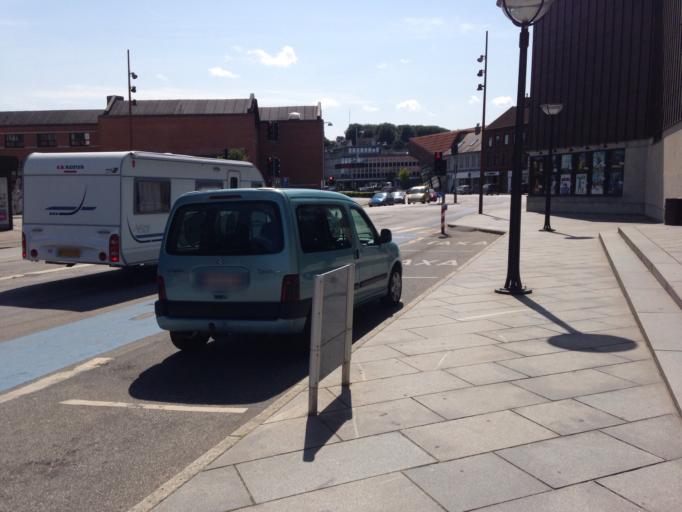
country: DK
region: South Denmark
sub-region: Vejle Kommune
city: Vejle
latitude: 55.7054
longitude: 9.5332
